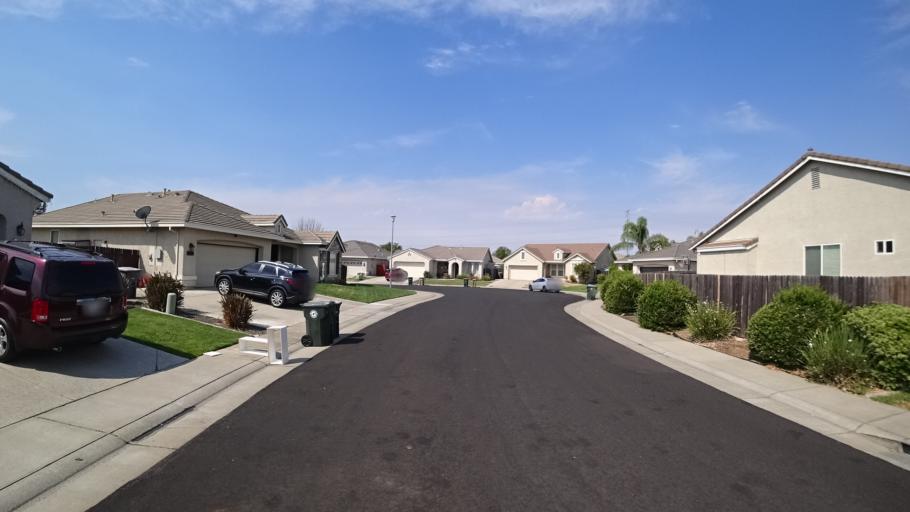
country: US
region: California
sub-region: Sacramento County
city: Laguna
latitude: 38.3890
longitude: -121.4497
